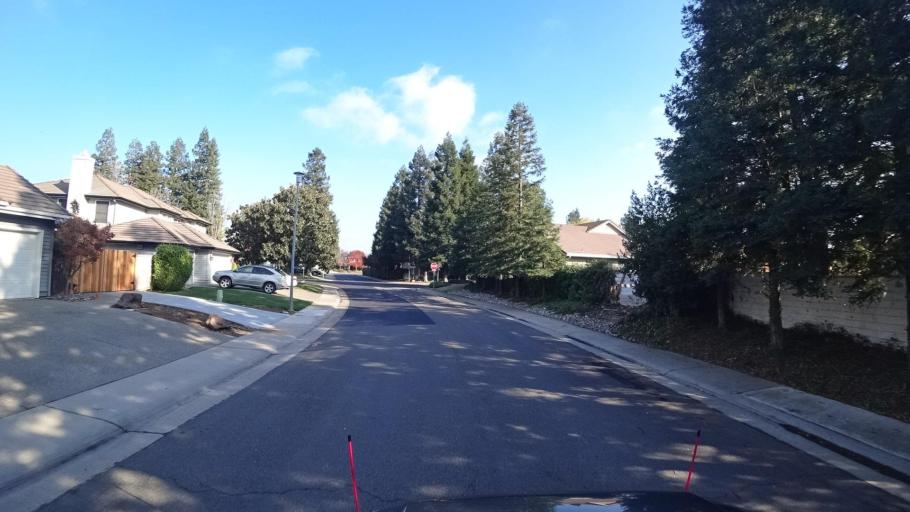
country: US
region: California
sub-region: Sacramento County
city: Elk Grove
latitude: 38.4142
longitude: -121.3555
